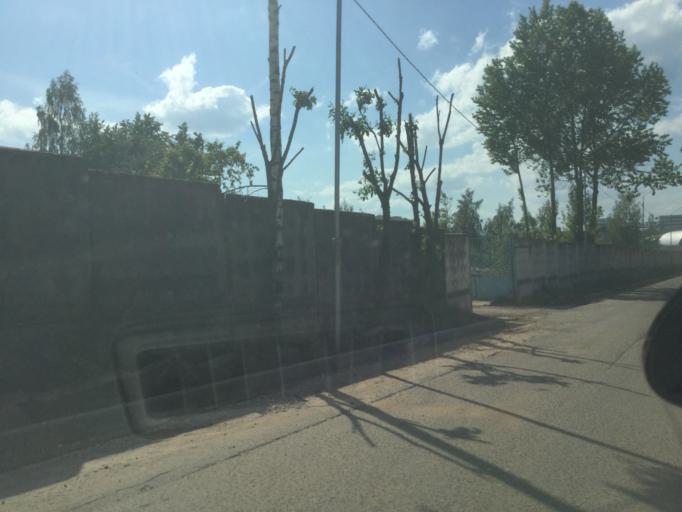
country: BY
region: Vitebsk
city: Vitebsk
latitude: 55.1643
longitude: 30.2420
